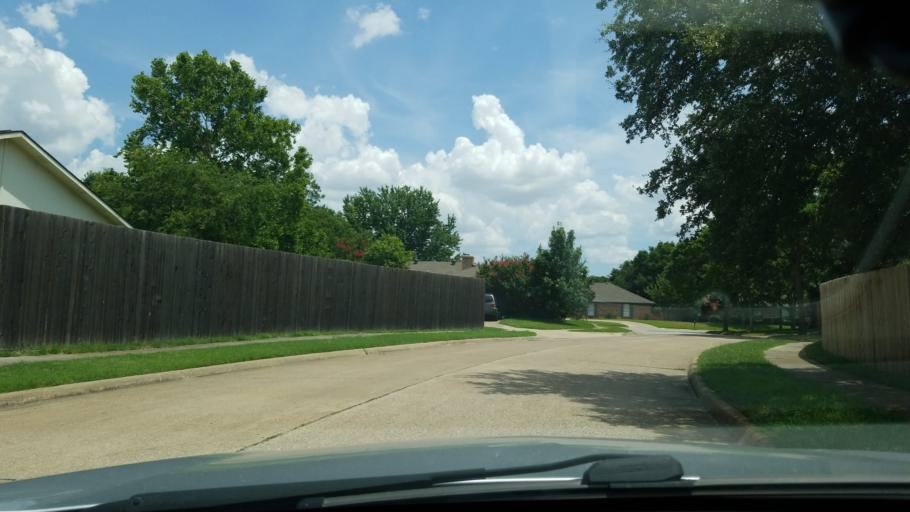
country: US
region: Texas
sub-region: Dallas County
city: Coppell
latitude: 32.9623
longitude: -96.9825
